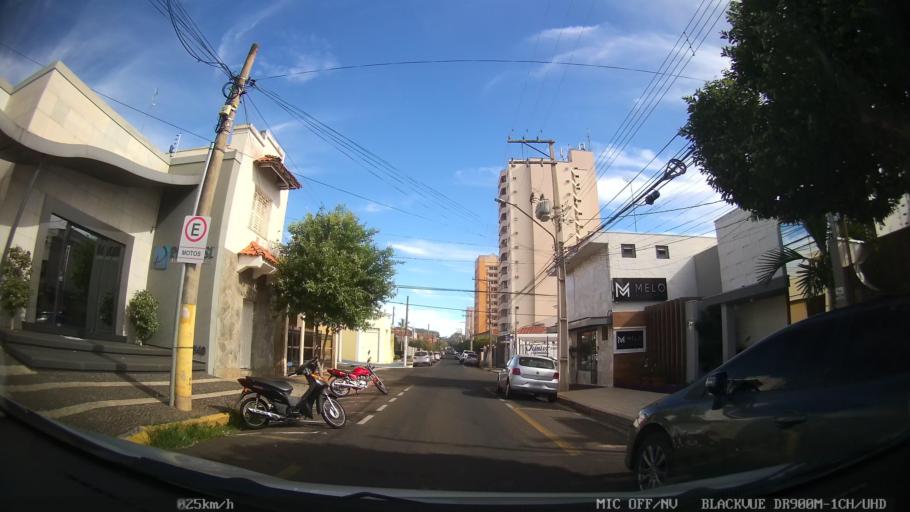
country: BR
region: Sao Paulo
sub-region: Catanduva
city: Catanduva
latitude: -21.1338
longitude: -48.9756
